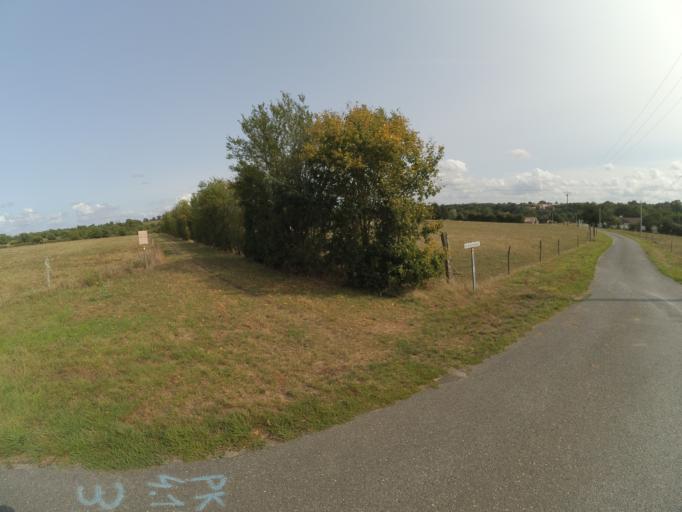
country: FR
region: Pays de la Loire
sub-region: Departement de la Loire-Atlantique
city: Boussay
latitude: 47.0364
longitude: -1.1635
